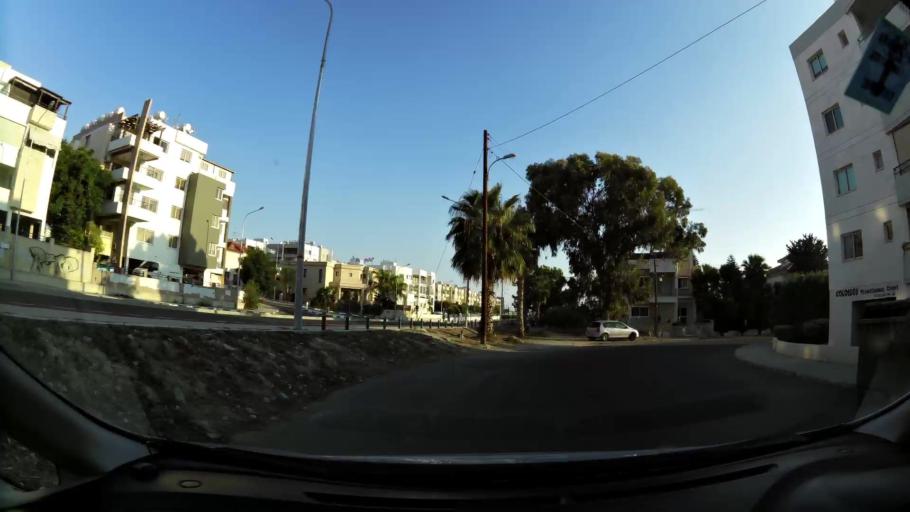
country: CY
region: Larnaka
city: Larnaca
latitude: 34.9202
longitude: 33.6001
